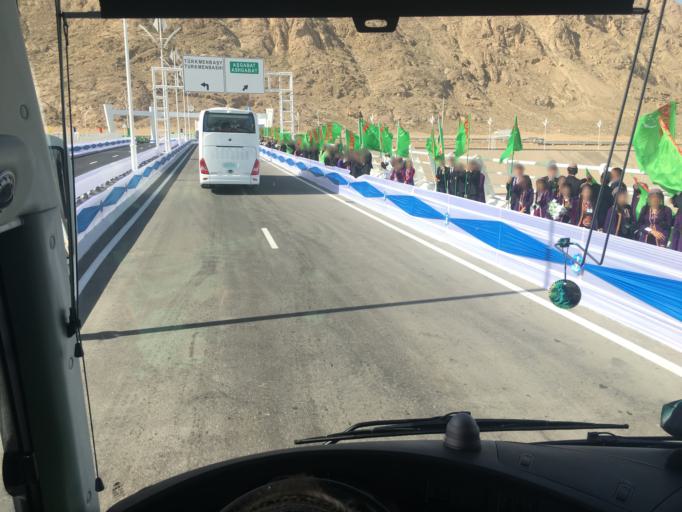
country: TM
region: Balkan
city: Turkmenbasy
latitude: 40.0062
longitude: 53.0241
